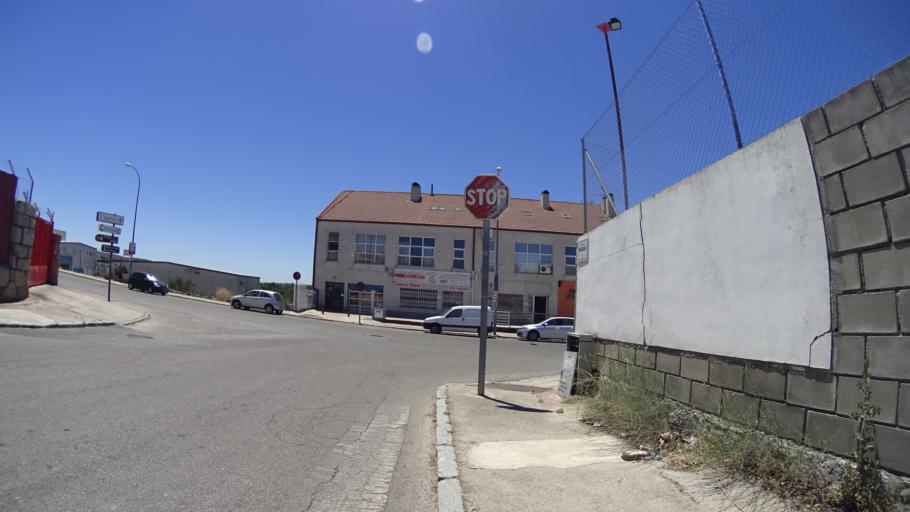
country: ES
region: Madrid
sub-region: Provincia de Madrid
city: Alpedrete
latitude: 40.6604
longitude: -4.0190
